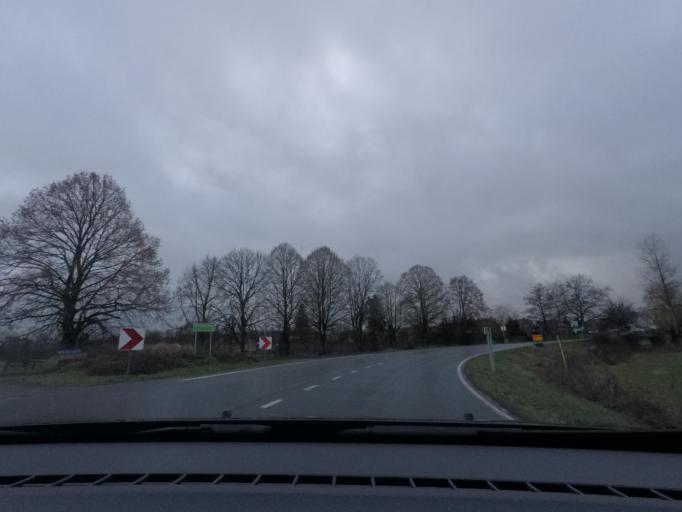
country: BE
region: Wallonia
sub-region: Province du Luxembourg
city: Tintigny
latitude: 49.6974
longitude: 5.4922
